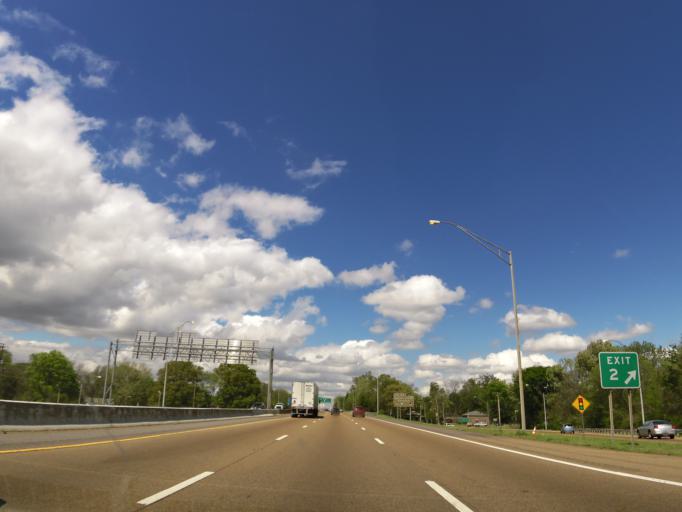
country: US
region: Tennessee
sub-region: Shelby County
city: Memphis
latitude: 35.1686
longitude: -90.0185
